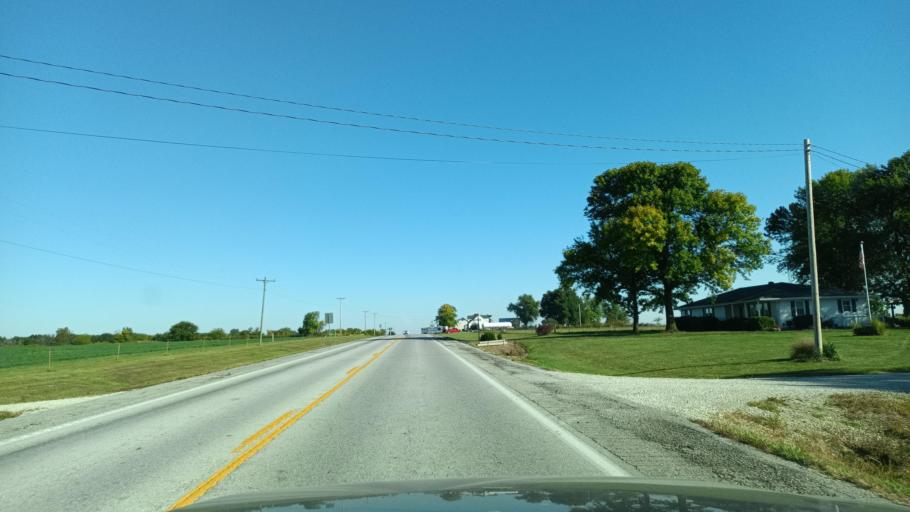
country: US
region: Missouri
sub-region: Audrain County
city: Vandalia
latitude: 39.3507
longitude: -91.6427
